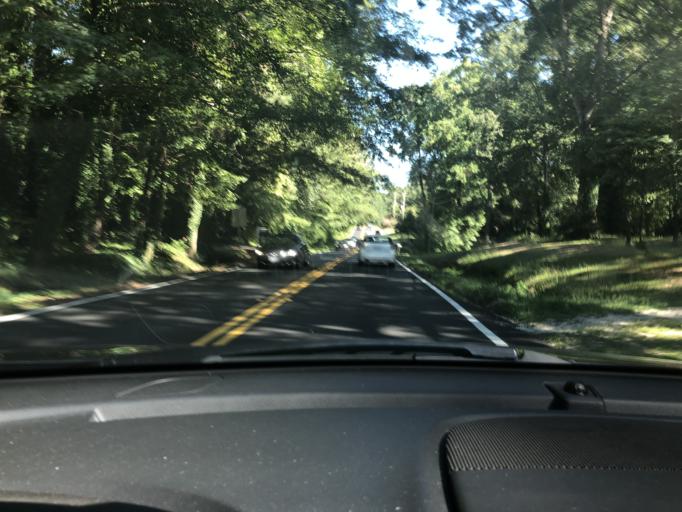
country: US
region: Georgia
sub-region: Gwinnett County
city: Lawrenceville
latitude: 33.9439
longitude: -83.9704
